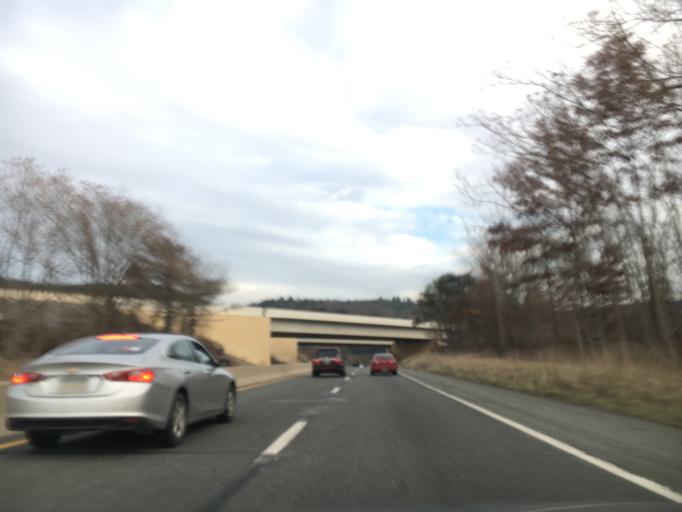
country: US
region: Pennsylvania
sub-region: Carbon County
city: Weissport East
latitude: 40.8188
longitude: -75.6792
